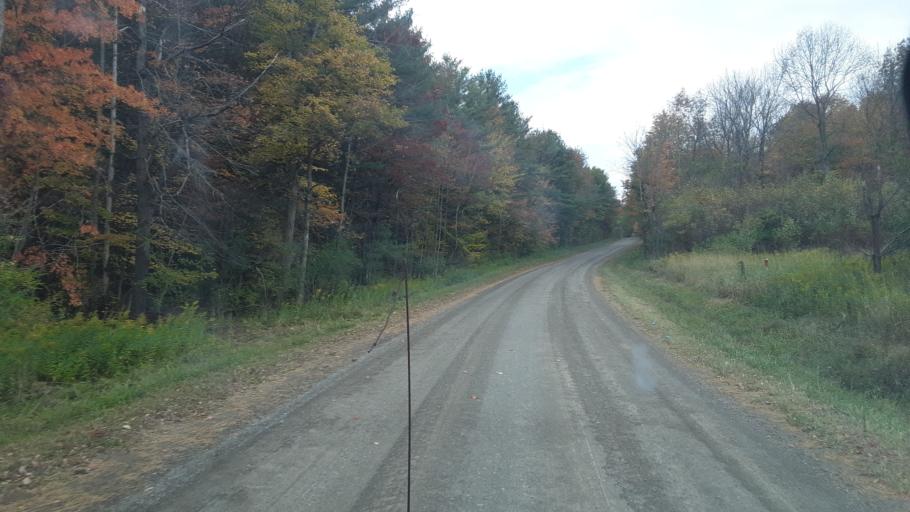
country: US
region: New York
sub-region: Allegany County
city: Alfred
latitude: 42.3880
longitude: -77.8663
